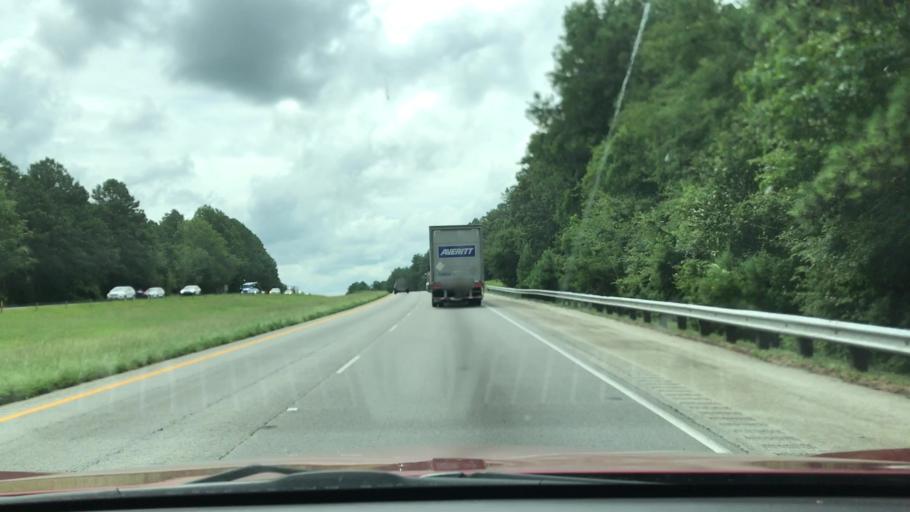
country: US
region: South Carolina
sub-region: Laurens County
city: Joanna
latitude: 34.3853
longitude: -81.6856
